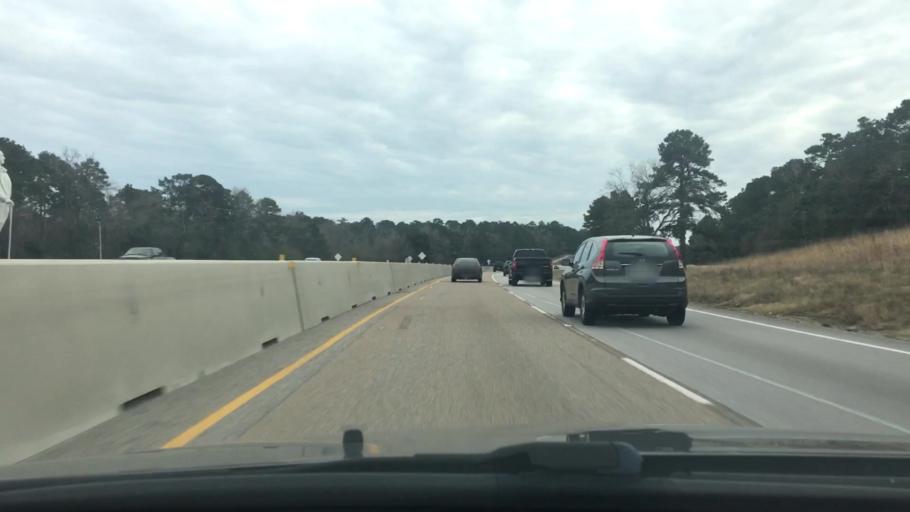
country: US
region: Texas
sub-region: Walker County
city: Huntsville
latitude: 30.6620
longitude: -95.5120
